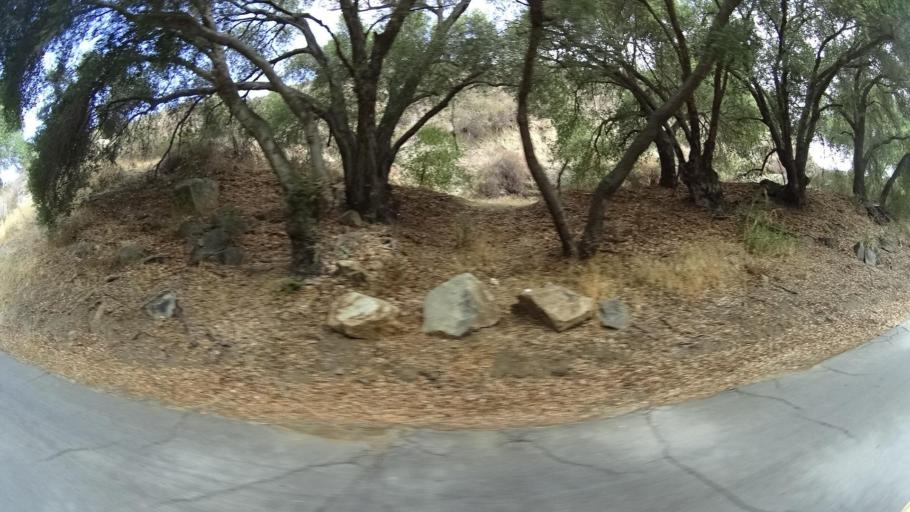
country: US
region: California
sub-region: San Diego County
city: Fallbrook
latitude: 33.4153
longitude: -117.2463
